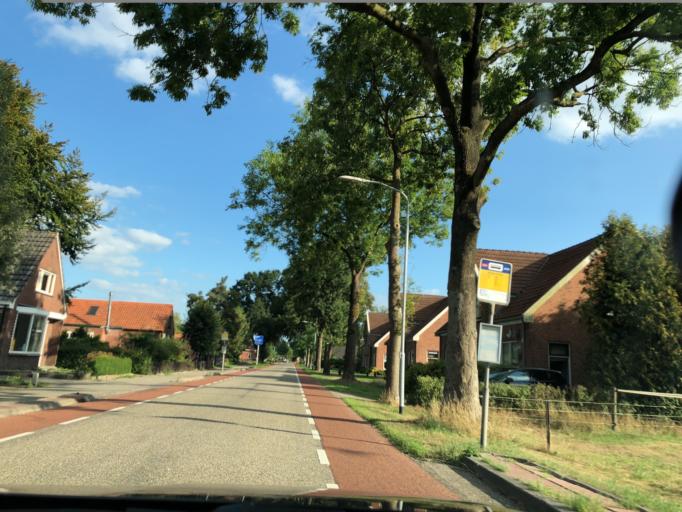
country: NL
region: Groningen
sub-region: Gemeente Vlagtwedde
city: Sellingen
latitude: 53.0122
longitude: 7.1819
